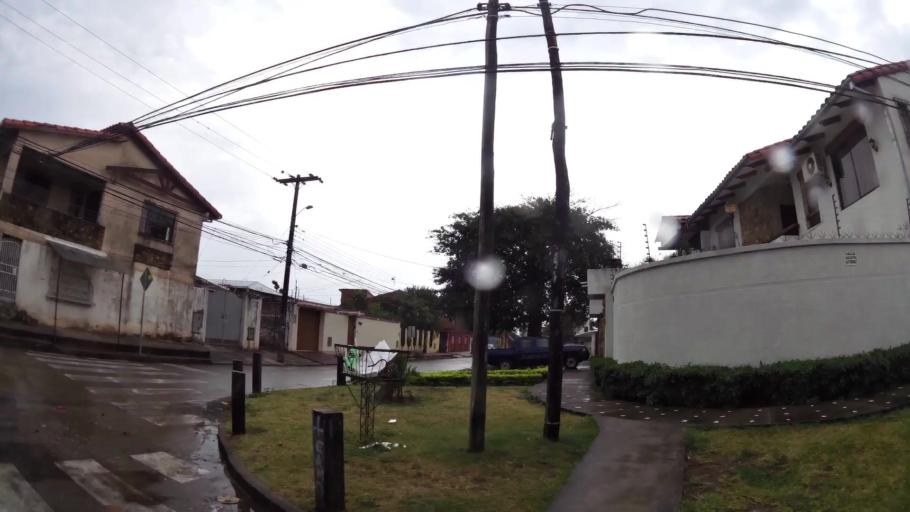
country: BO
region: Santa Cruz
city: Santa Cruz de la Sierra
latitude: -17.7636
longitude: -63.1538
